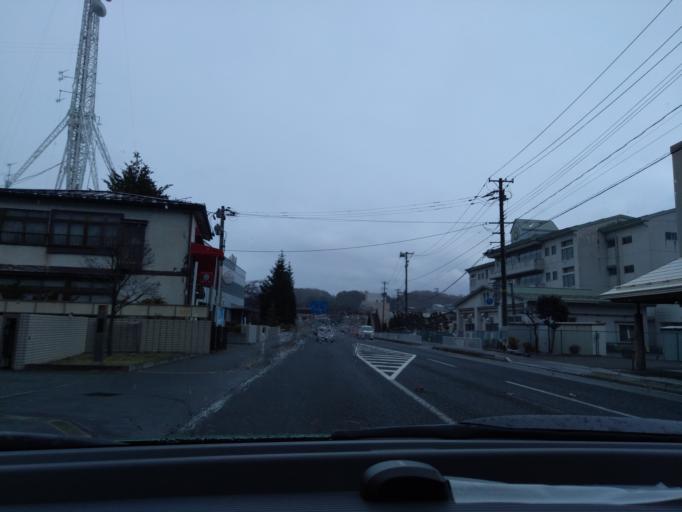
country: JP
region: Iwate
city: Morioka-shi
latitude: 39.7195
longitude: 141.1374
